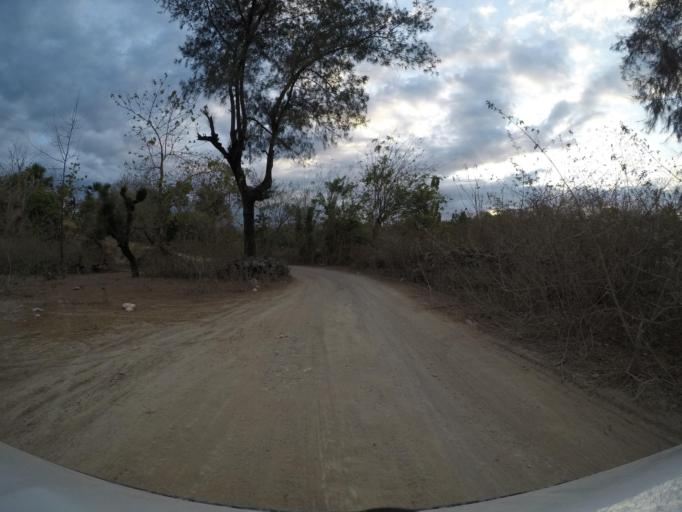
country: TL
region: Bobonaro
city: Maliana
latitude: -8.9137
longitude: 125.2151
